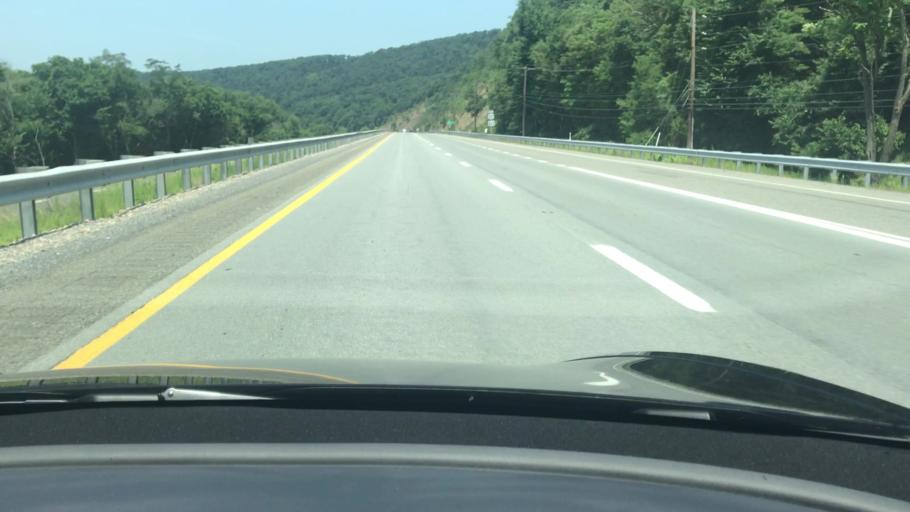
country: US
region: Pennsylvania
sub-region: Perry County
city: Newport
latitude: 40.5578
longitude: -77.1624
